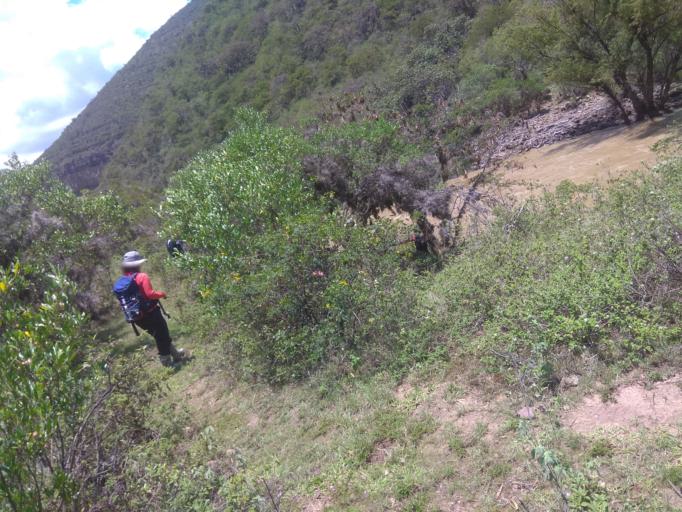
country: CO
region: Boyaca
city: Socha Viejo
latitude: 5.9968
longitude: -72.7194
